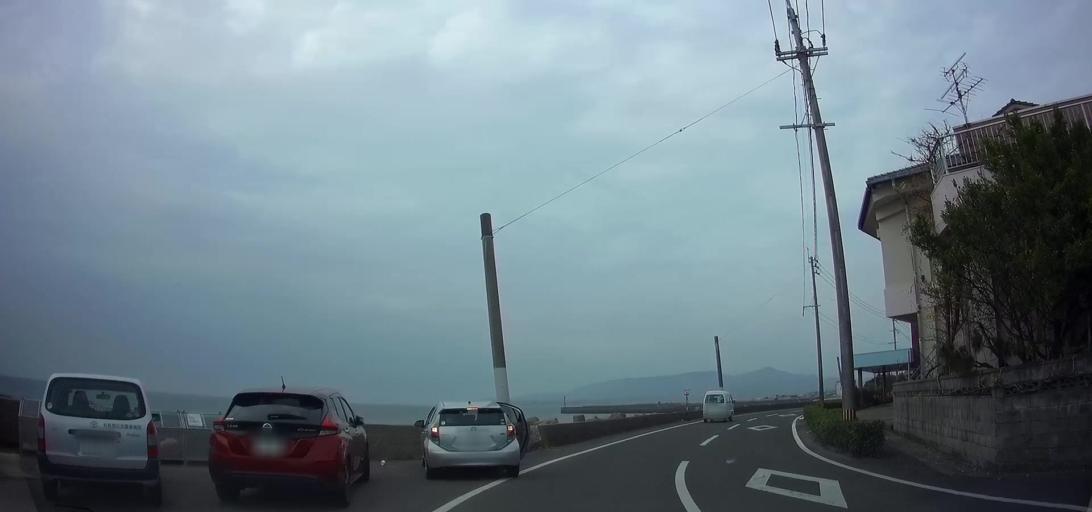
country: JP
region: Nagasaki
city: Shimabara
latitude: 32.6523
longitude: 130.2971
